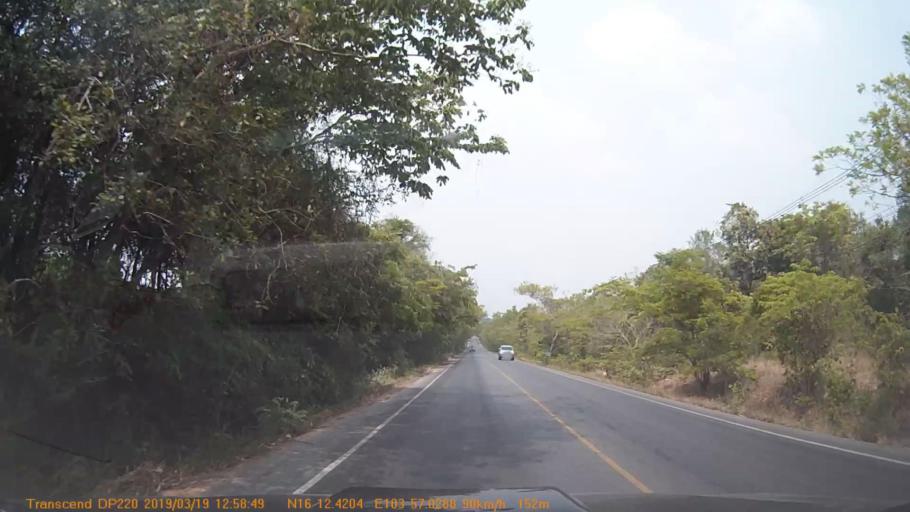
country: TH
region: Roi Et
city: Waeng
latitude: 16.2072
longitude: 103.9505
